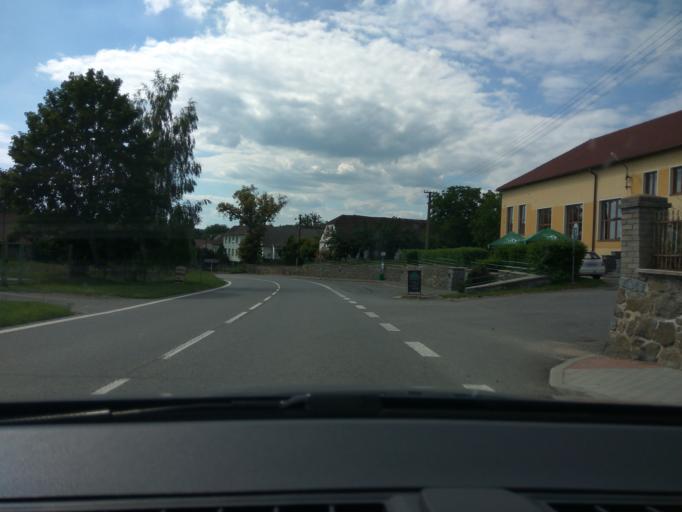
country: CZ
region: Jihocesky
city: Kovarov
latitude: 49.4742
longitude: 14.2925
